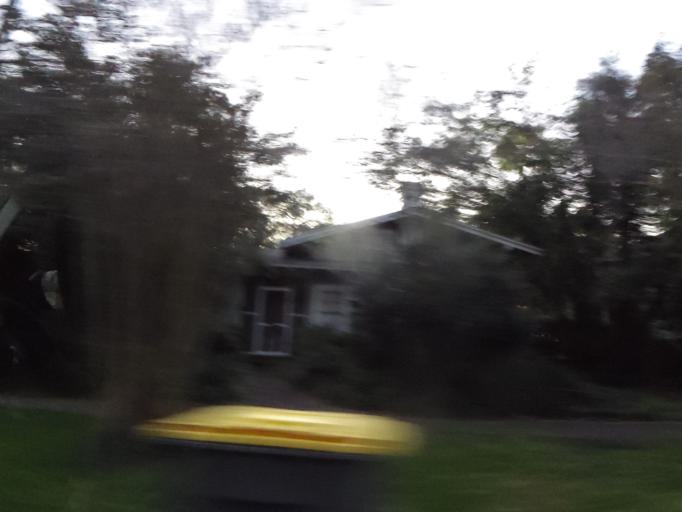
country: US
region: Florida
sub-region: Duval County
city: Jacksonville
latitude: 30.3044
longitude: -81.7041
